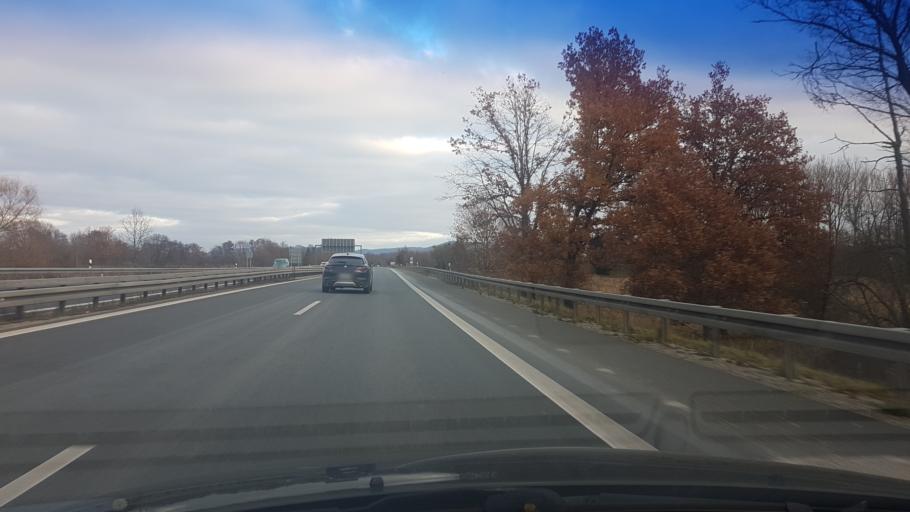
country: DE
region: Bavaria
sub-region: Upper Franconia
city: Gundelsheim
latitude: 49.9323
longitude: 10.9286
